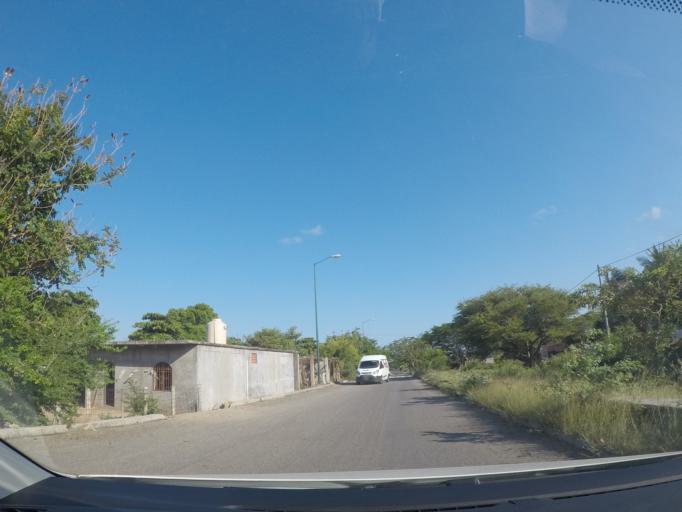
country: MX
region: Oaxaca
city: Juchitan de Zaragoza
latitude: 16.4201
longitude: -95.0273
